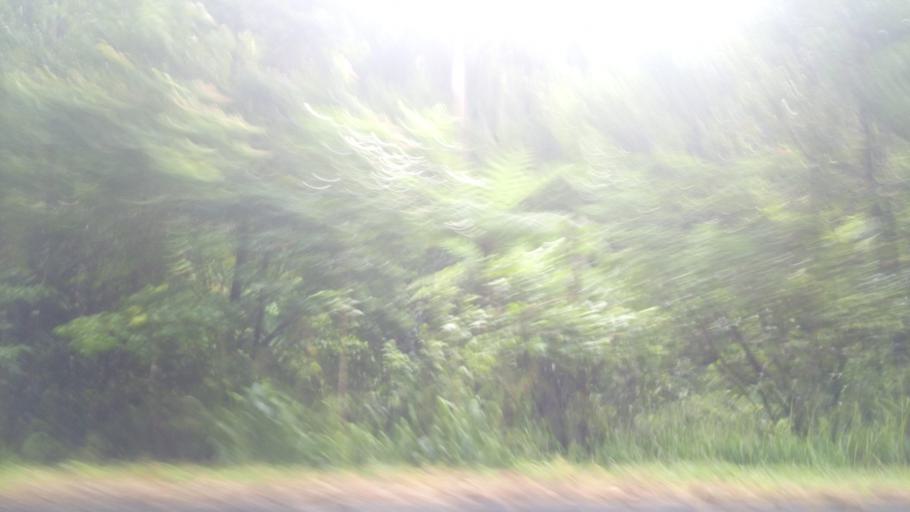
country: AU
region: Queensland
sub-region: Tablelands
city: Ravenshoe
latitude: -17.5826
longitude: 145.6951
